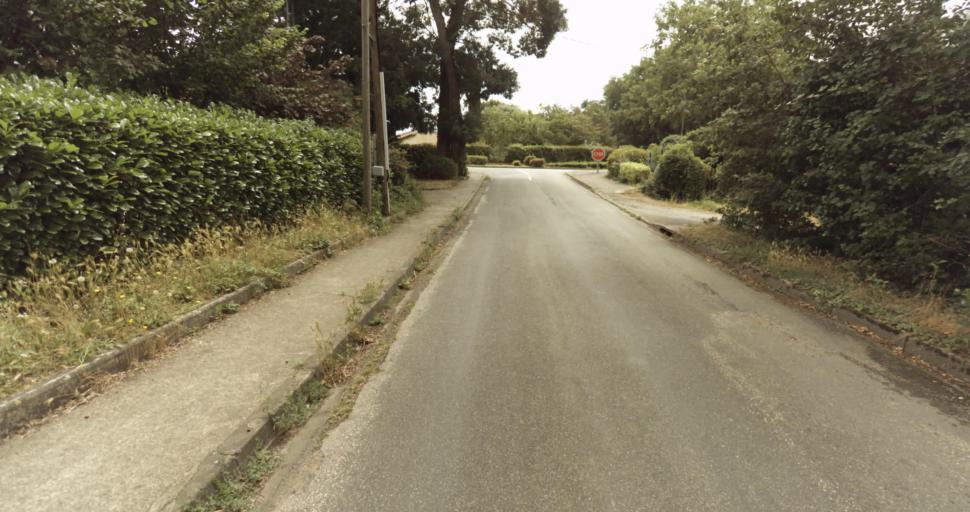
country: FR
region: Midi-Pyrenees
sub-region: Departement de la Haute-Garonne
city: Fontenilles
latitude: 43.5546
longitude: 1.1913
